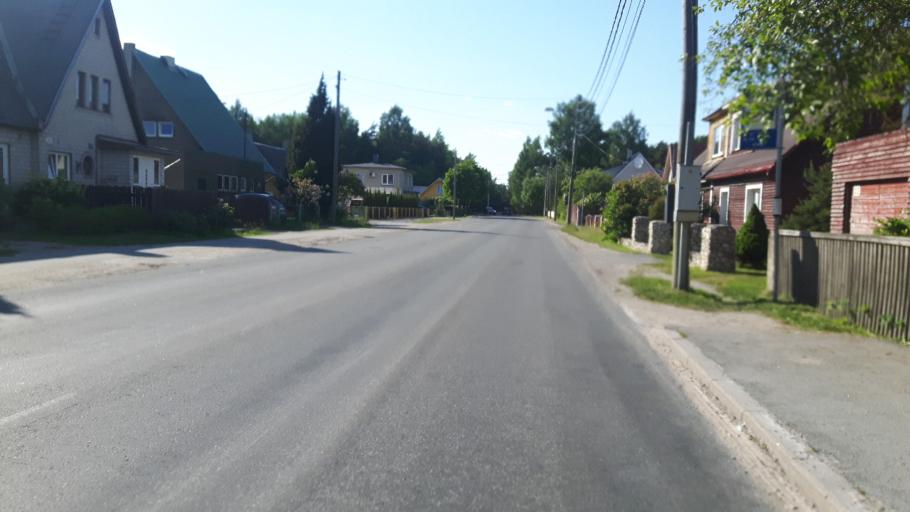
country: EE
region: Paernumaa
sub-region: Paernu linn
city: Parnu
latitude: 58.3594
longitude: 24.5592
